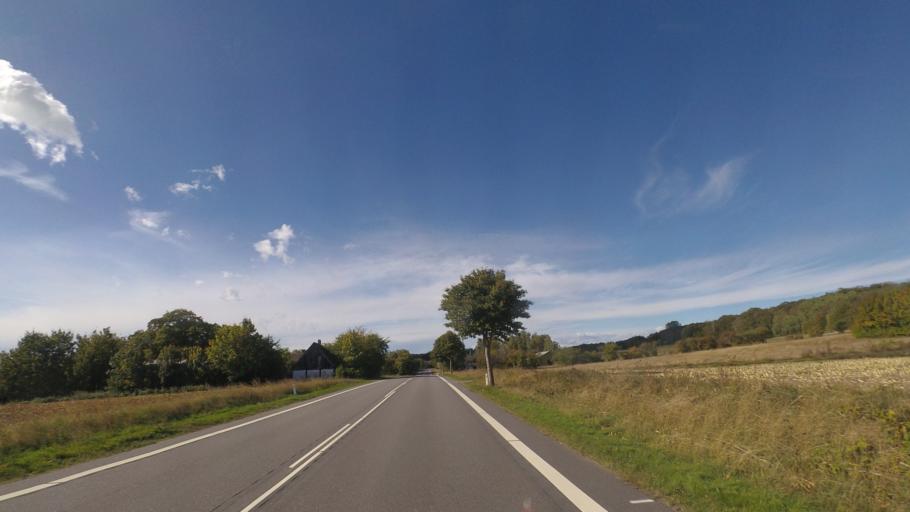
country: DK
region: Capital Region
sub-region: Bornholm Kommune
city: Ronne
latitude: 55.0786
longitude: 14.7647
